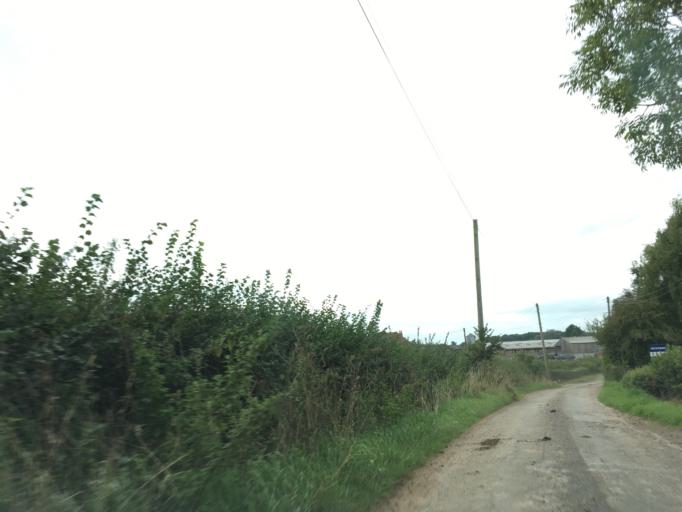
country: GB
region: England
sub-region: South Gloucestershire
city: Falfield
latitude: 51.6450
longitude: -2.4658
